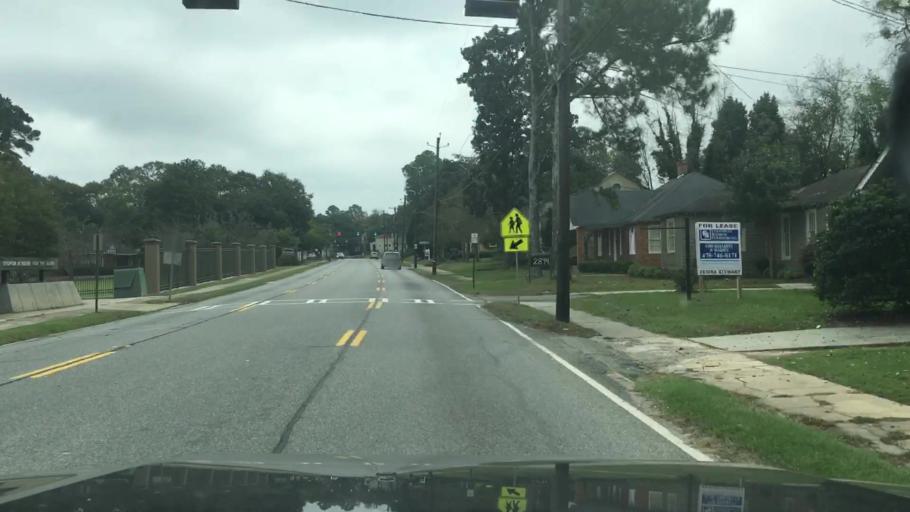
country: US
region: Georgia
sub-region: Bibb County
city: Macon
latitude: 32.8472
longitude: -83.6694
